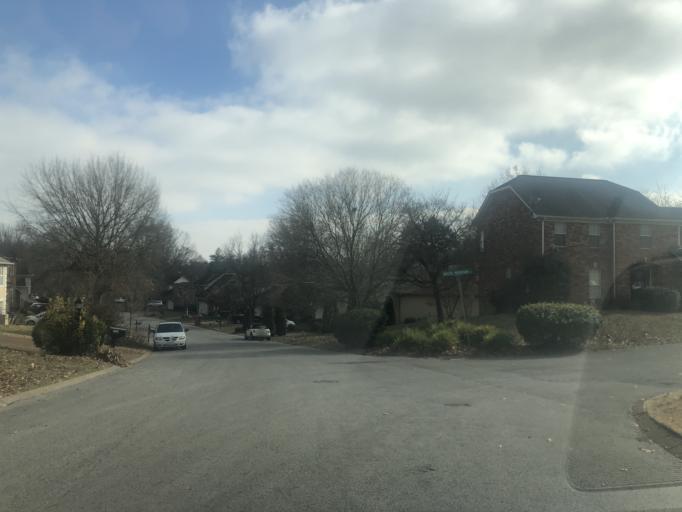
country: US
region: Tennessee
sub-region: Rutherford County
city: La Vergne
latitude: 36.0834
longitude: -86.6557
